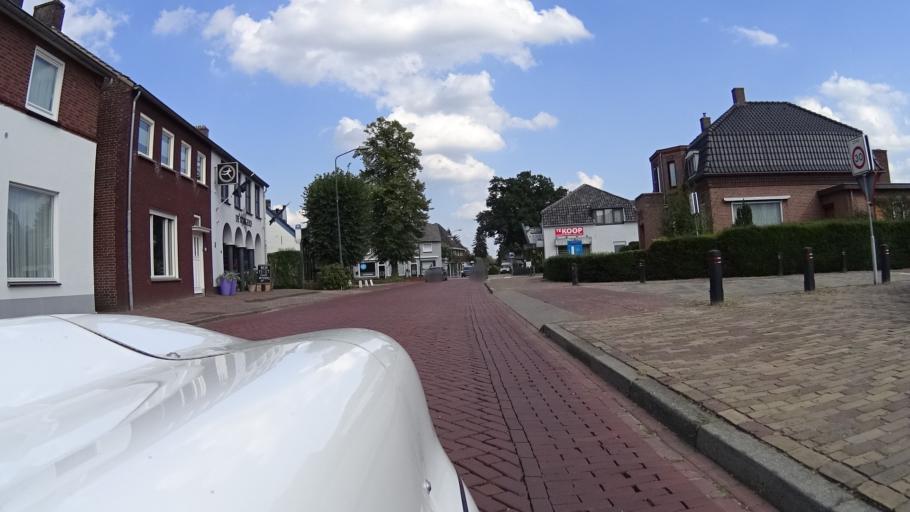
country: NL
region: North Brabant
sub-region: Gemeente Sint Anthonis
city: Sint Anthonis
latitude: 51.6271
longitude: 5.8864
